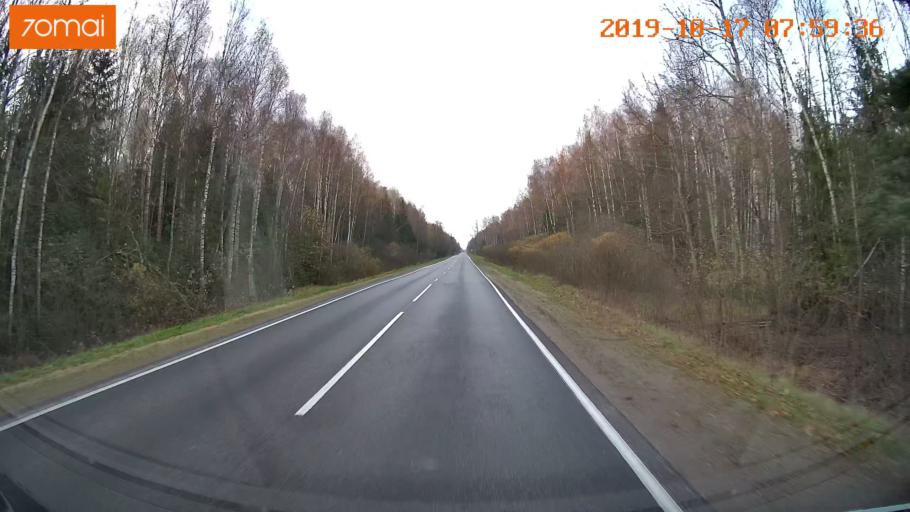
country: RU
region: Vladimir
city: Bavleny
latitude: 56.3918
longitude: 39.5352
